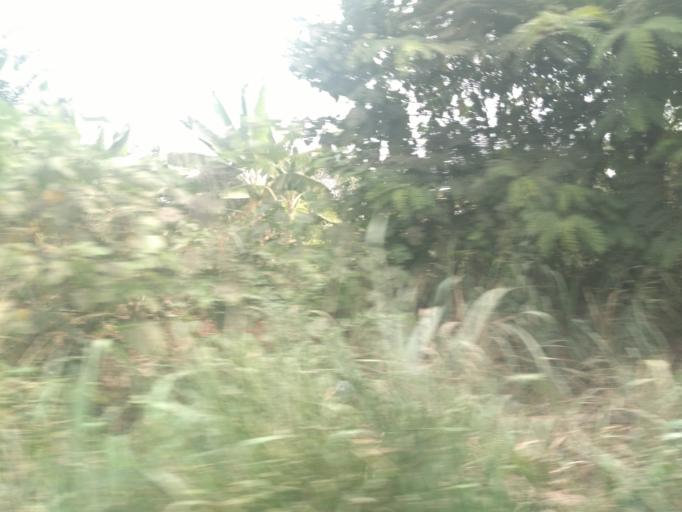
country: GH
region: Ashanti
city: Kumasi
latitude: 6.6885
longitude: -1.6326
